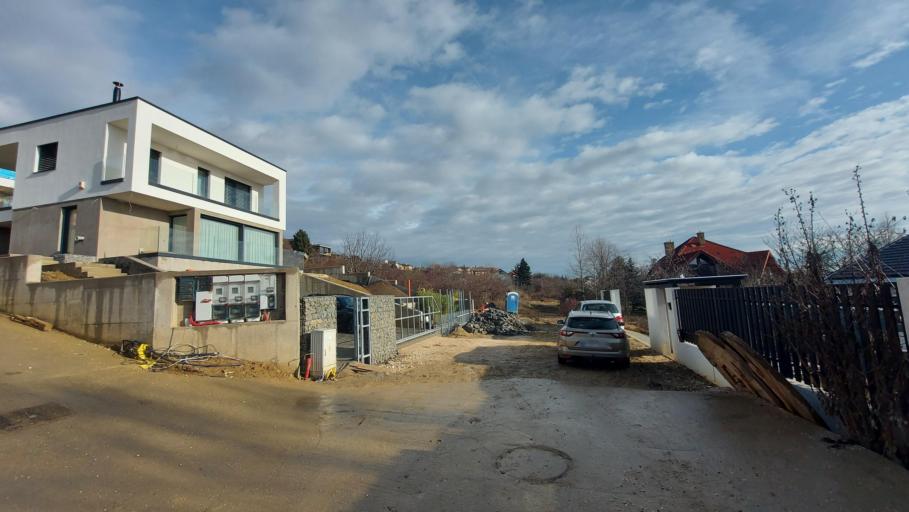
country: HU
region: Pest
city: Budaors
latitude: 47.4636
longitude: 18.9442
